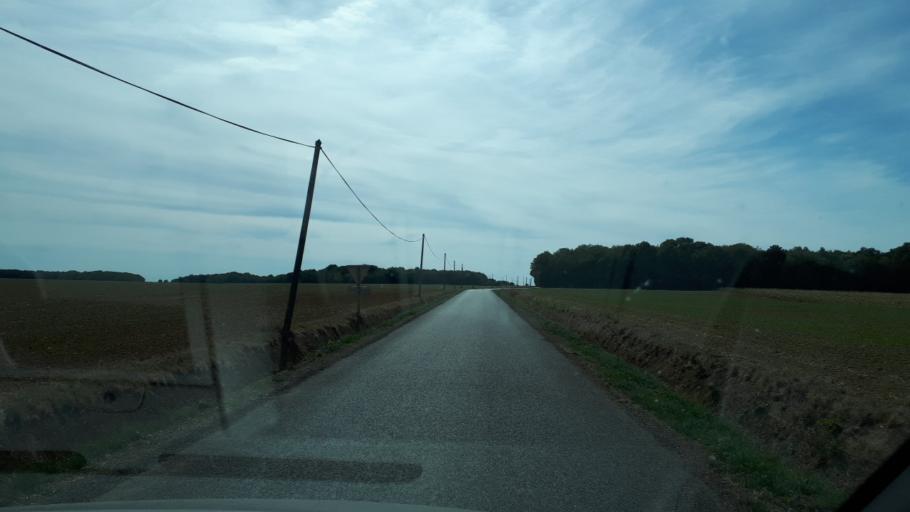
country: FR
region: Centre
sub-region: Departement du Loir-et-Cher
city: Montoire-sur-le-Loir
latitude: 47.7022
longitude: 0.8364
